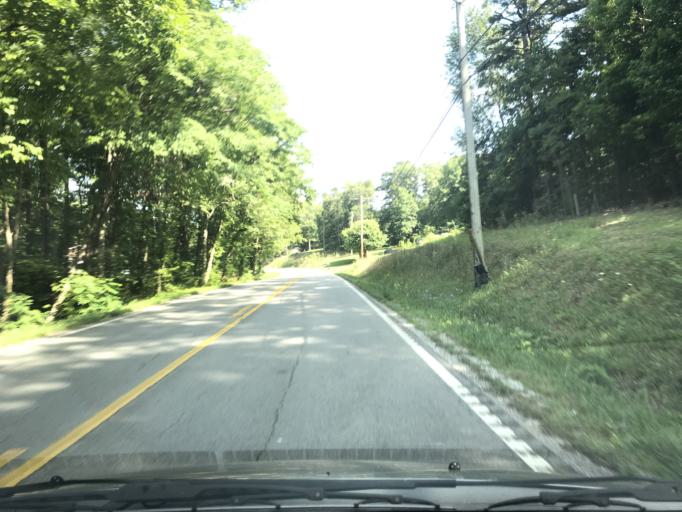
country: US
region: Tennessee
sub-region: Hamilton County
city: Lakesite
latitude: 35.2287
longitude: -85.0617
